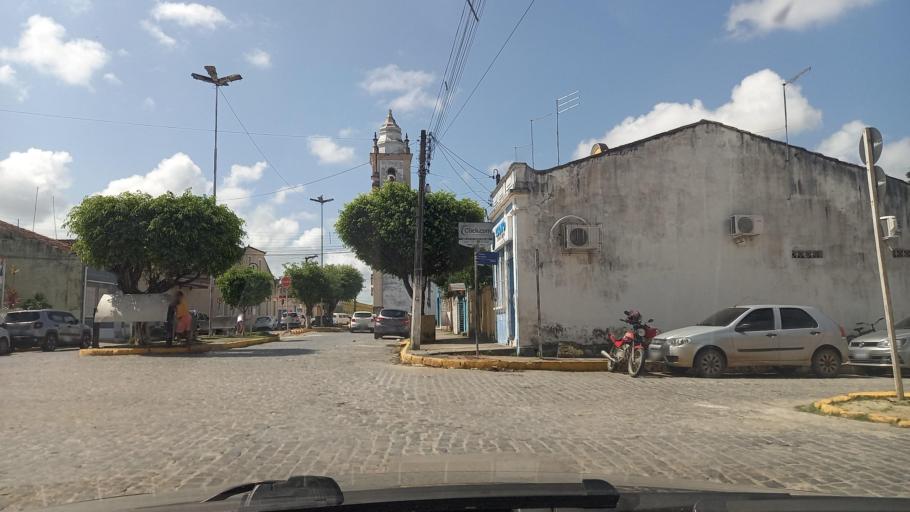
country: BR
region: Pernambuco
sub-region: Goiana
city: Goiana
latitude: -7.5597
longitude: -34.9975
